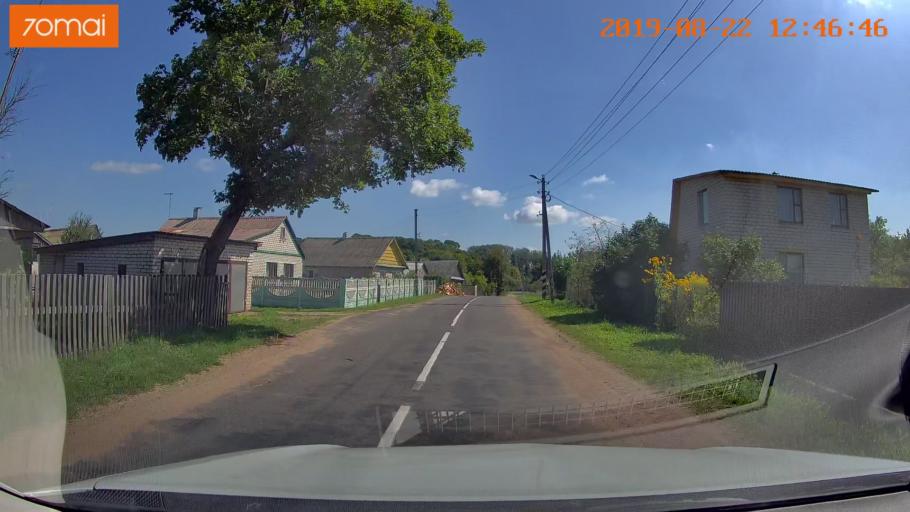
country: BY
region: Minsk
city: Prawdzinski
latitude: 53.4583
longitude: 27.6332
